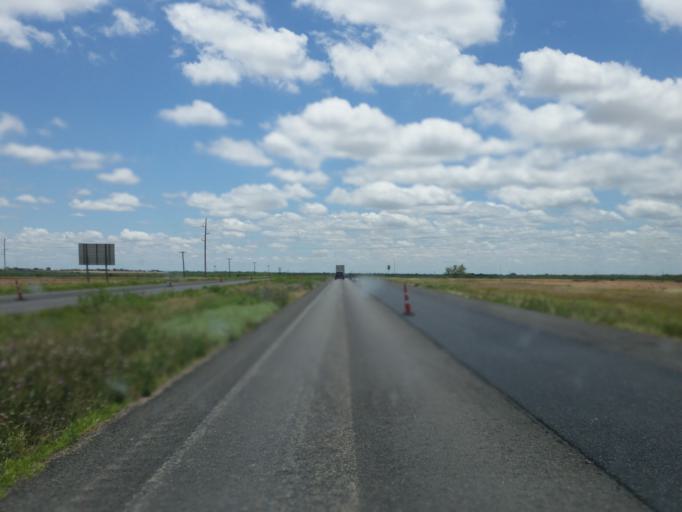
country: US
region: Texas
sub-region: Scurry County
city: Snyder
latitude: 32.7780
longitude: -100.9432
